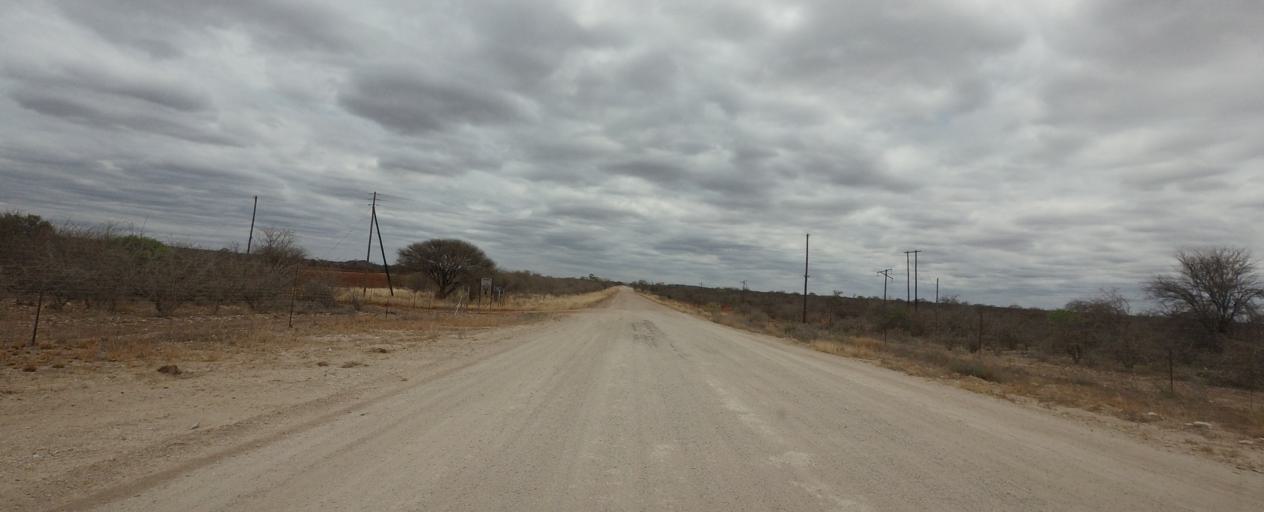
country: BW
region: Central
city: Mathathane
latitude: -22.7060
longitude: 28.5961
